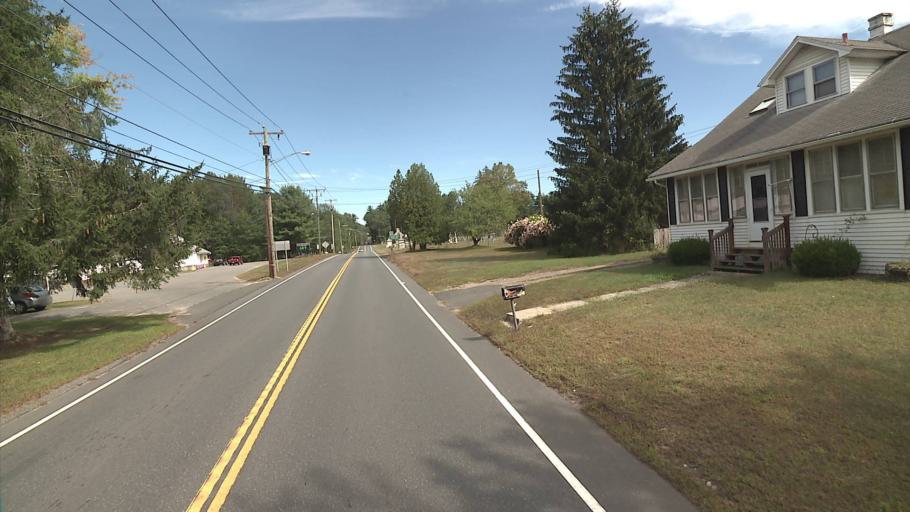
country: US
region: Connecticut
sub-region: Tolland County
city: Stafford Springs
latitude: 41.9634
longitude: -72.3154
